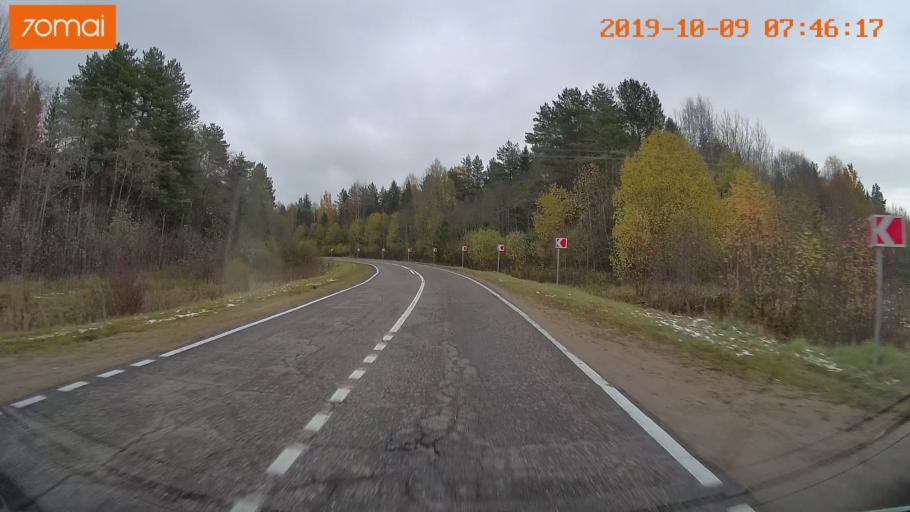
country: RU
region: Jaroslavl
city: Kukoboy
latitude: 58.6555
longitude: 39.7847
